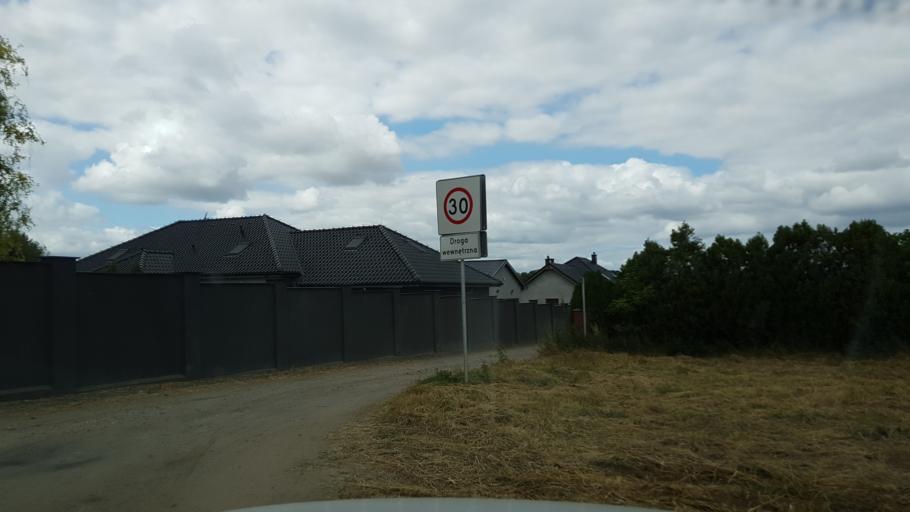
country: PL
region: West Pomeranian Voivodeship
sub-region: Powiat mysliborski
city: Mysliborz
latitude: 52.9301
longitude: 14.8814
